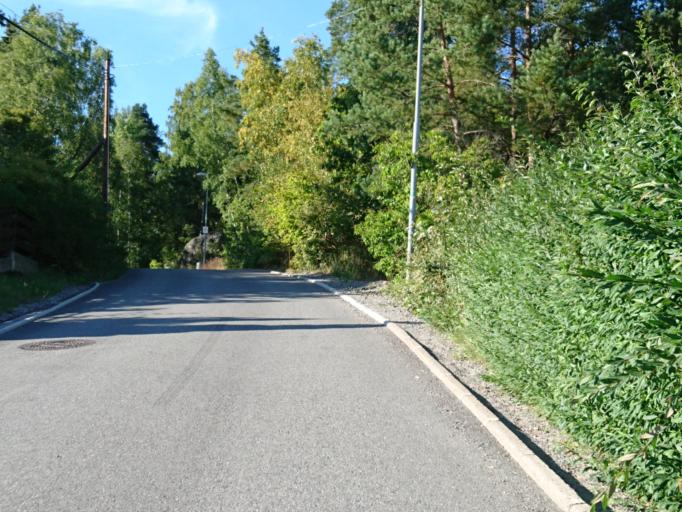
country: SE
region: Stockholm
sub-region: Huddinge Kommun
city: Huddinge
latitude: 59.2558
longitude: 17.9924
